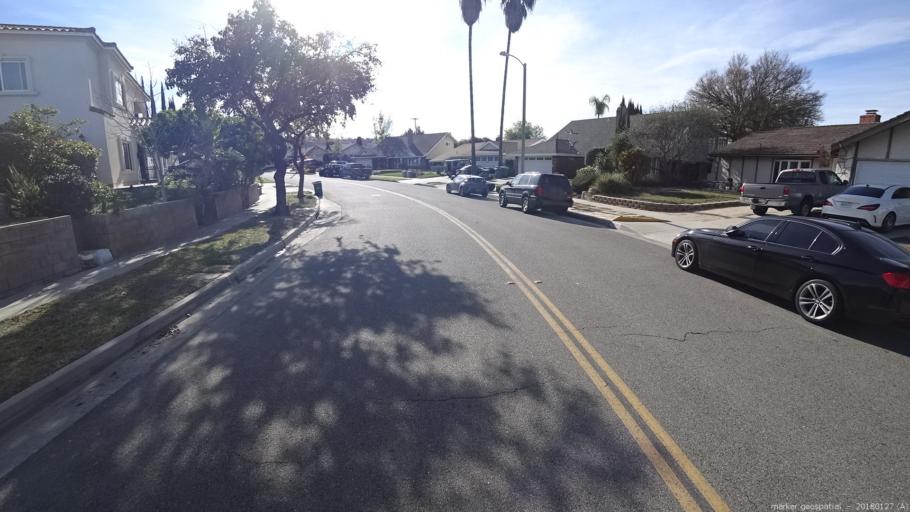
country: US
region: California
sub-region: Los Angeles County
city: Diamond Bar
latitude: 34.0263
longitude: -117.8103
